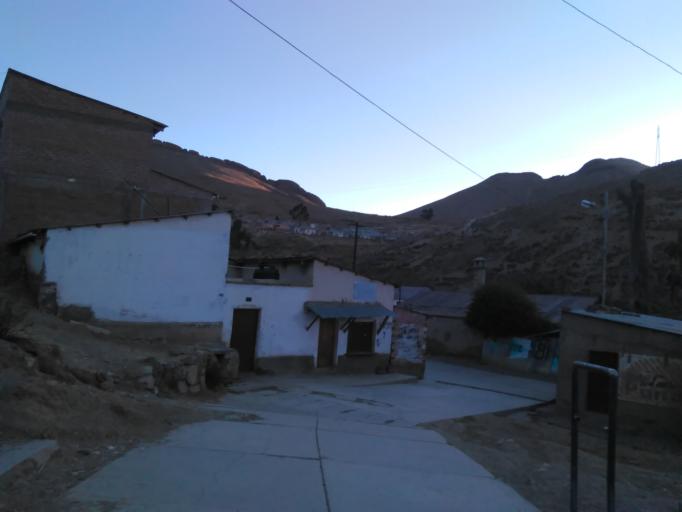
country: BO
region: Potosi
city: Llallagua
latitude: -18.4240
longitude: -66.5921
